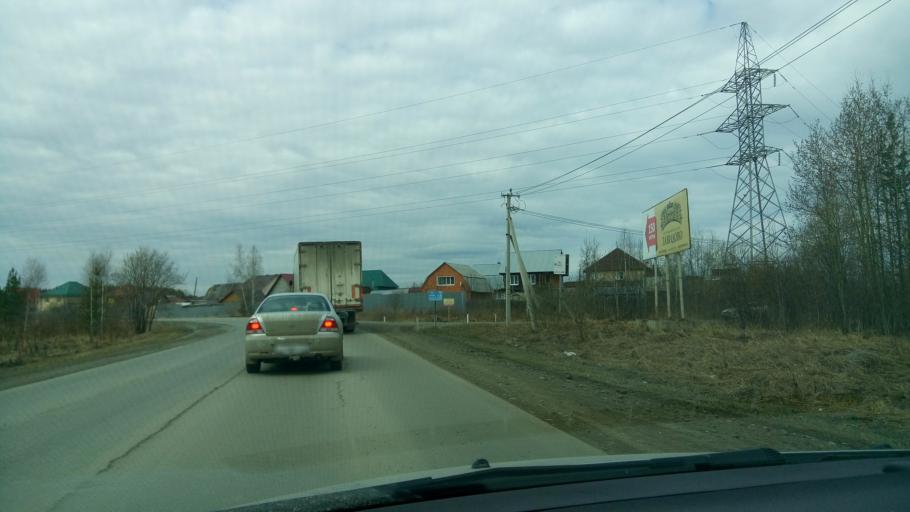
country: RU
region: Sverdlovsk
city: Verkhnyaya Pyshma
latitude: 56.9557
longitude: 60.6582
